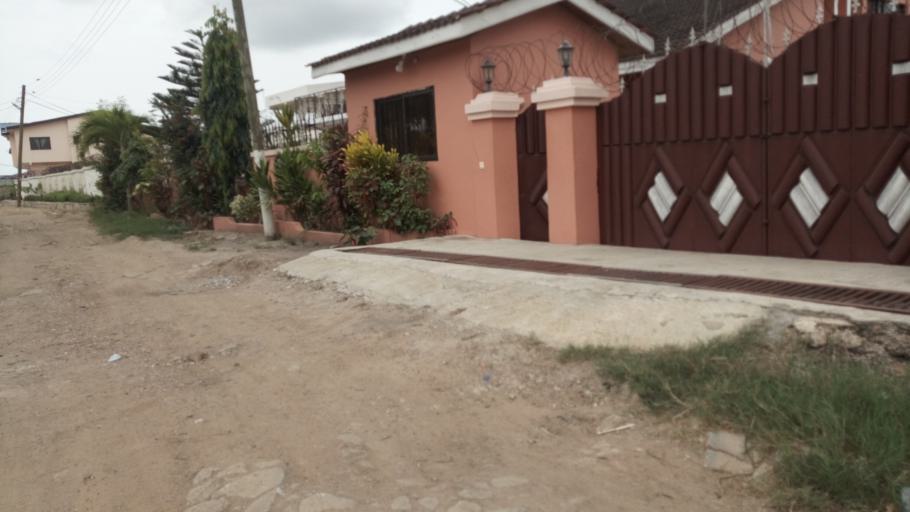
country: GH
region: Central
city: Winneba
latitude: 5.3834
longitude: -0.6396
